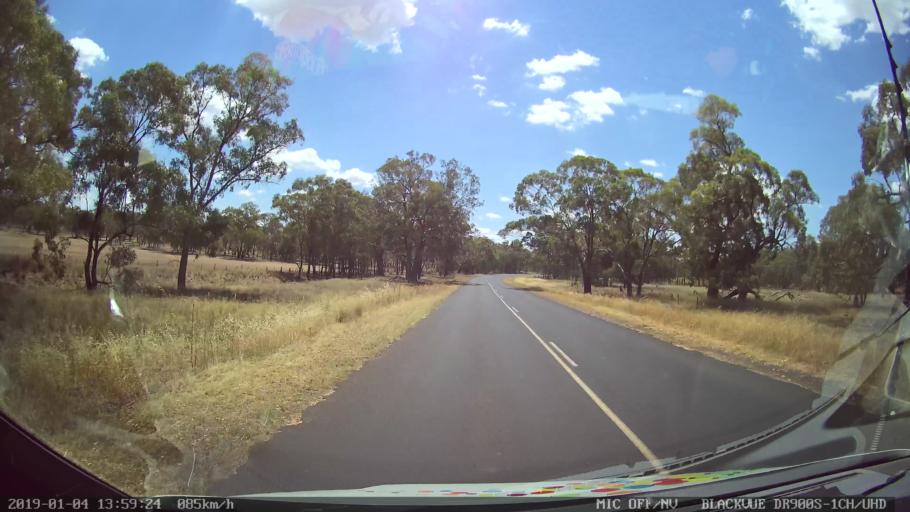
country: AU
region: New South Wales
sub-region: Dubbo Municipality
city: Dubbo
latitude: -32.3176
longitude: 148.5897
